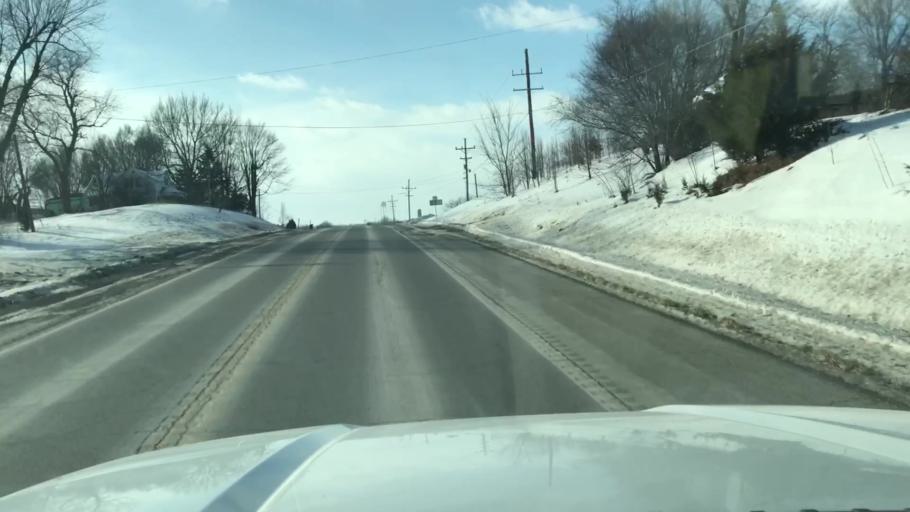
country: US
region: Missouri
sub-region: Nodaway County
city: Maryville
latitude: 40.3446
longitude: -94.7929
